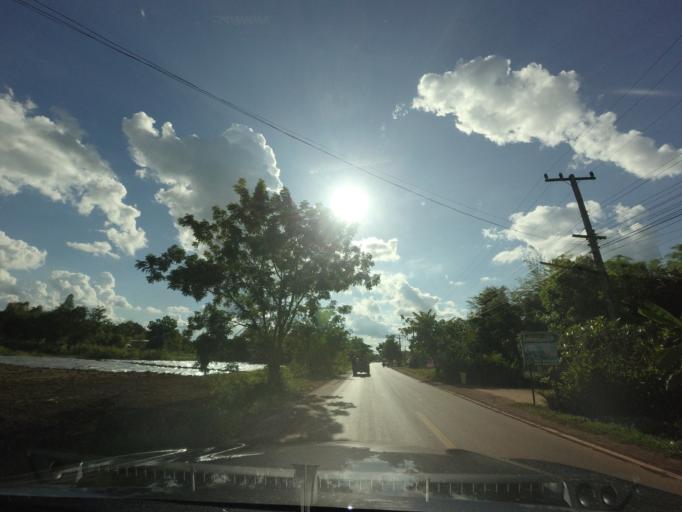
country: TH
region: Changwat Udon Thani
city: Ban Dung
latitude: 17.7450
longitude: 103.3228
